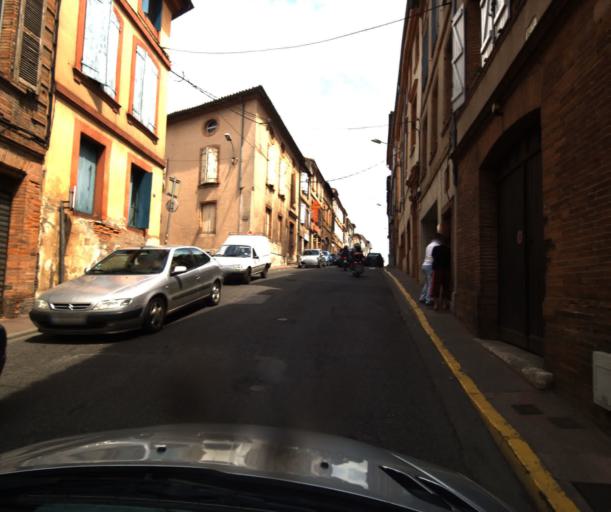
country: FR
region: Midi-Pyrenees
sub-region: Departement du Tarn-et-Garonne
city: Montauban
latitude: 44.0198
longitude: 1.3553
